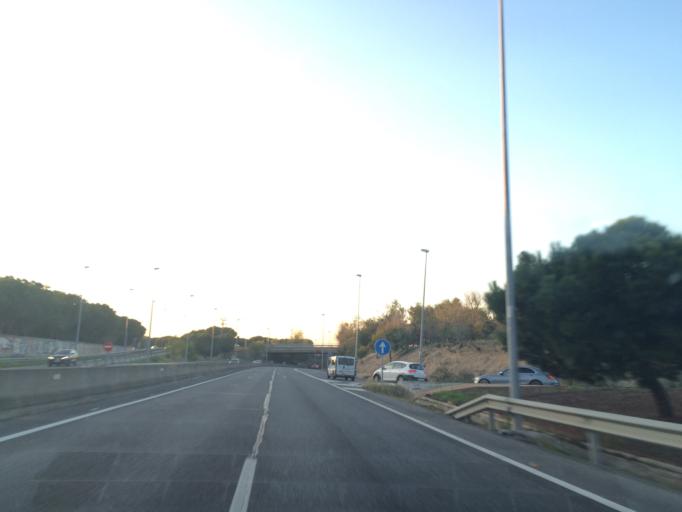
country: ES
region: Madrid
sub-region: Provincia de Madrid
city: Moncloa-Aravaca
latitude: 40.4483
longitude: -3.7603
